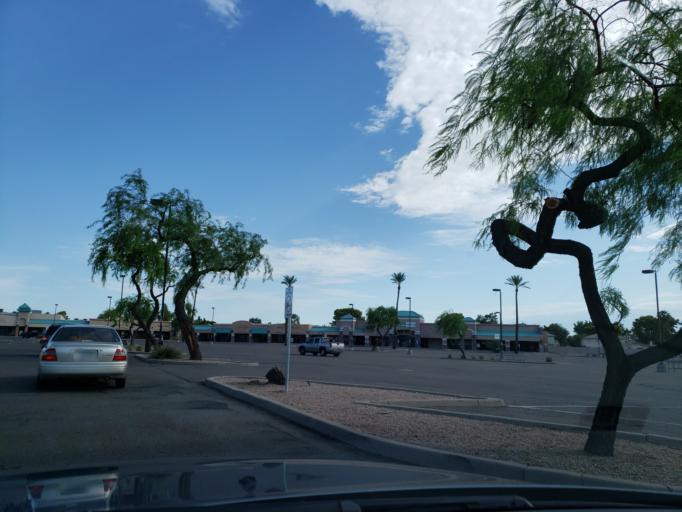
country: US
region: Arizona
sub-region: Maricopa County
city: Glendale
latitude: 33.5538
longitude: -112.1333
